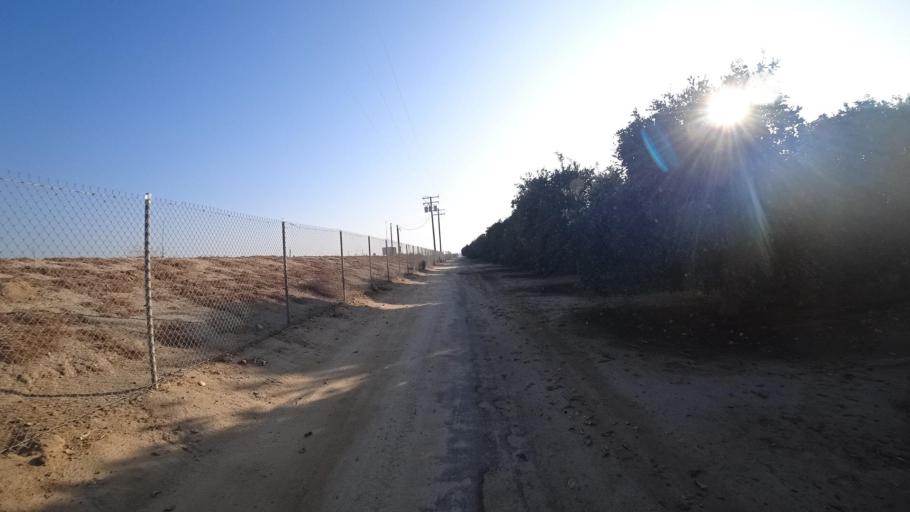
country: US
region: California
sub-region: Tulare County
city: Richgrove
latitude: 35.7763
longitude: -119.0950
